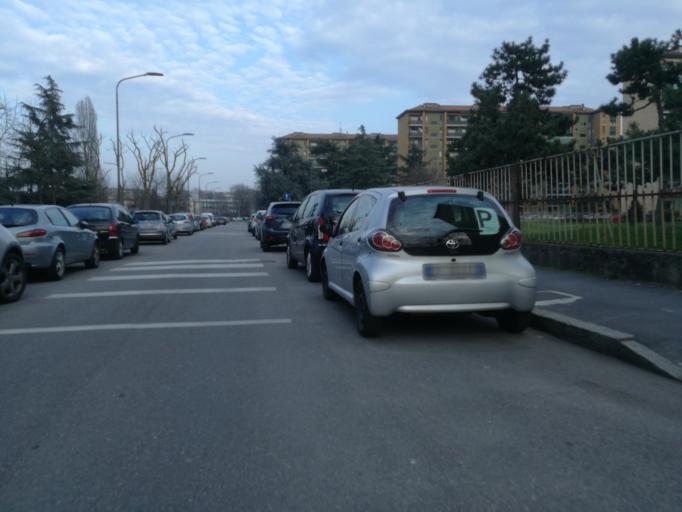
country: IT
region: Lombardy
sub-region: Citta metropolitana di Milano
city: Romano Banco
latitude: 45.4552
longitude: 9.1245
